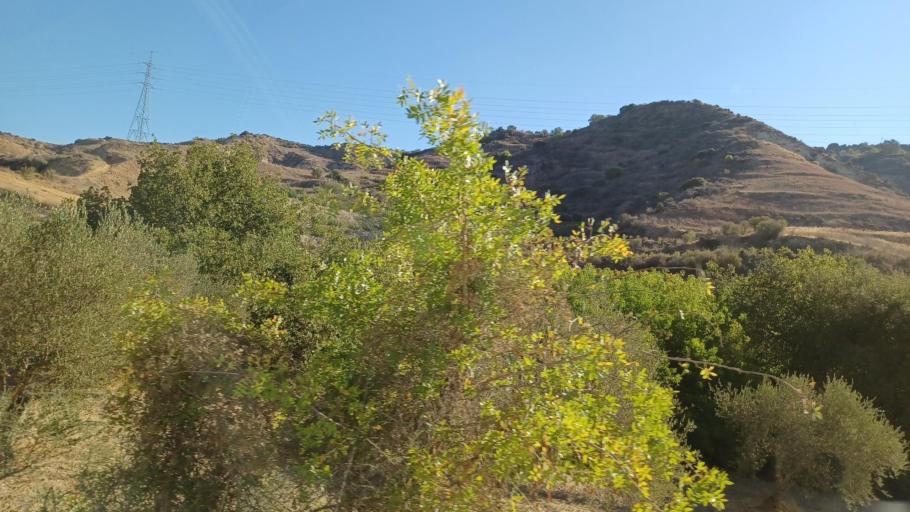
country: CY
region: Pafos
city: Polis
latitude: 34.9402
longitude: 32.4757
